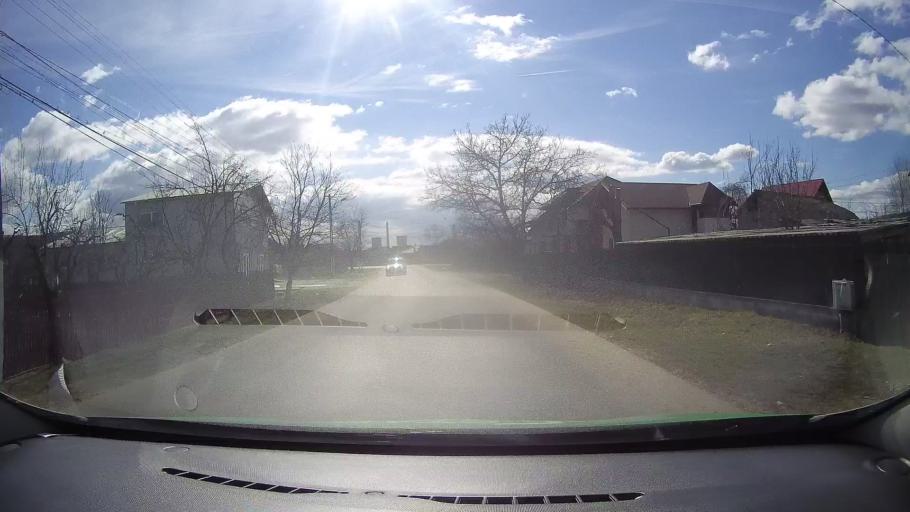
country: RO
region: Dambovita
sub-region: Comuna Vulcana-Pandele
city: Gura Vulcanei
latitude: 45.0249
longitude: 25.3949
